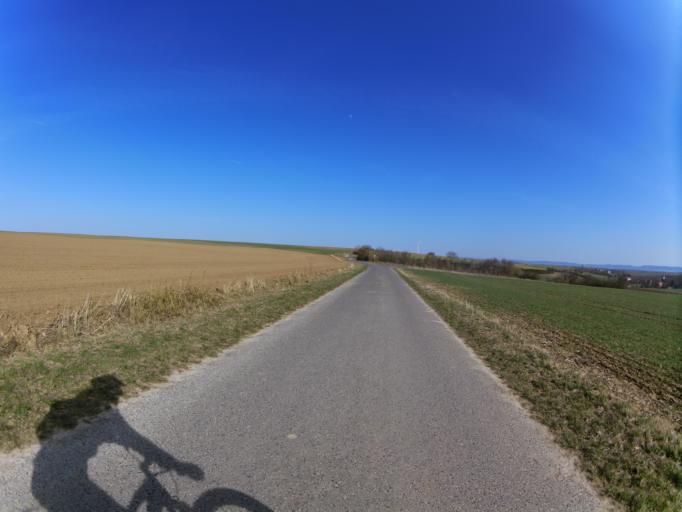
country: DE
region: Bavaria
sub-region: Regierungsbezirk Unterfranken
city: Prosselsheim
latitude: 49.8307
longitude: 10.1140
